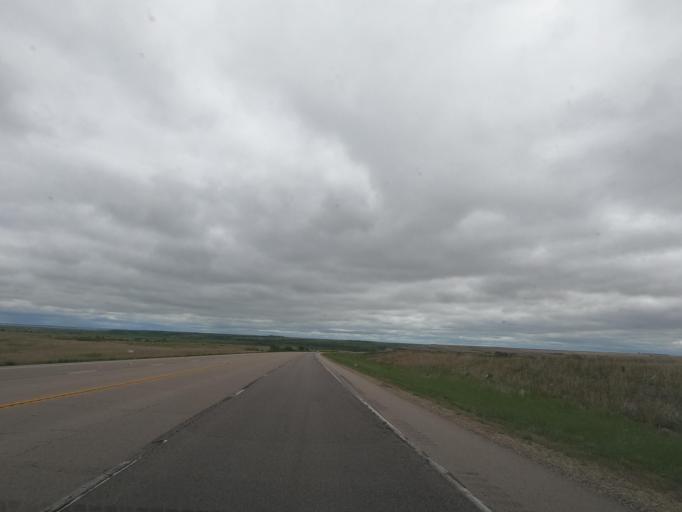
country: US
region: Kansas
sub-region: Greenwood County
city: Eureka
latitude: 37.6616
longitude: -96.4998
